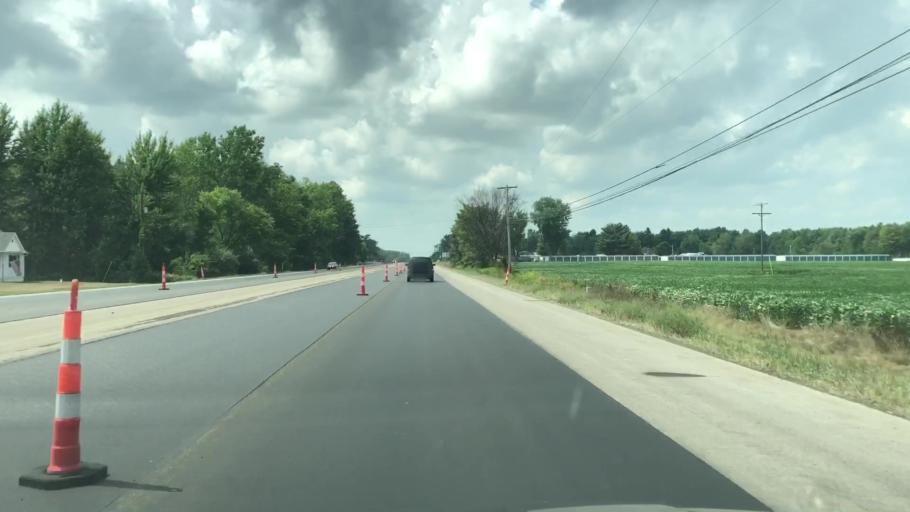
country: US
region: Michigan
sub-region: Isabella County
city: Mount Pleasant
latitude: 43.6117
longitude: -84.6938
